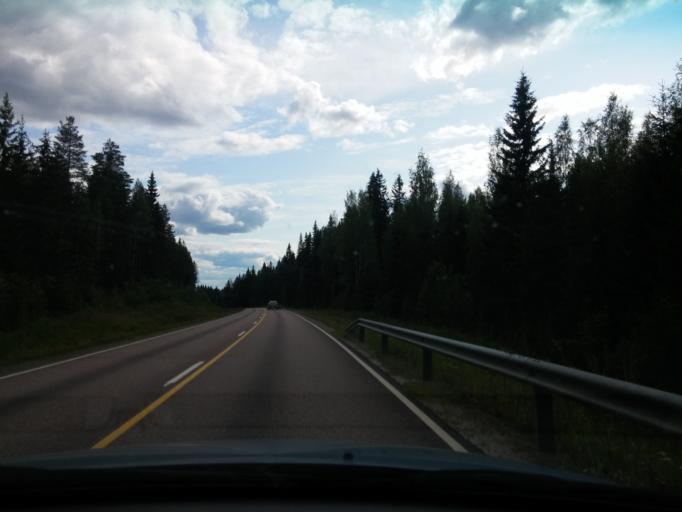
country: FI
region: Central Finland
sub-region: Keuruu
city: Multia
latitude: 62.3739
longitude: 24.7417
